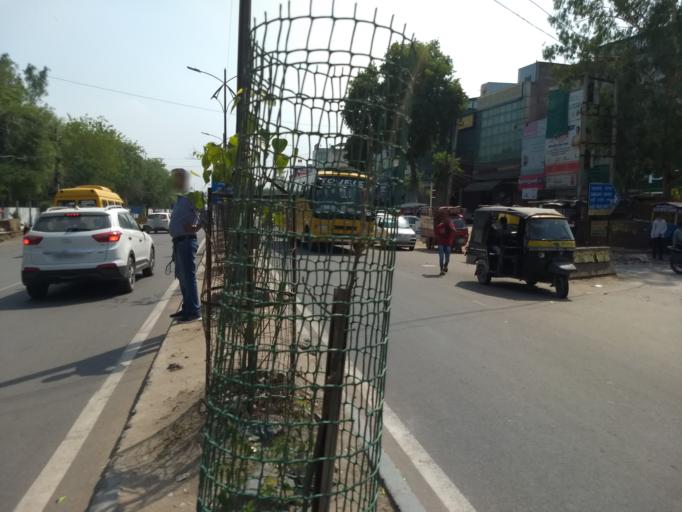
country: IN
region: Haryana
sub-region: Gurgaon
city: Gurgaon
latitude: 28.4752
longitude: 77.0436
